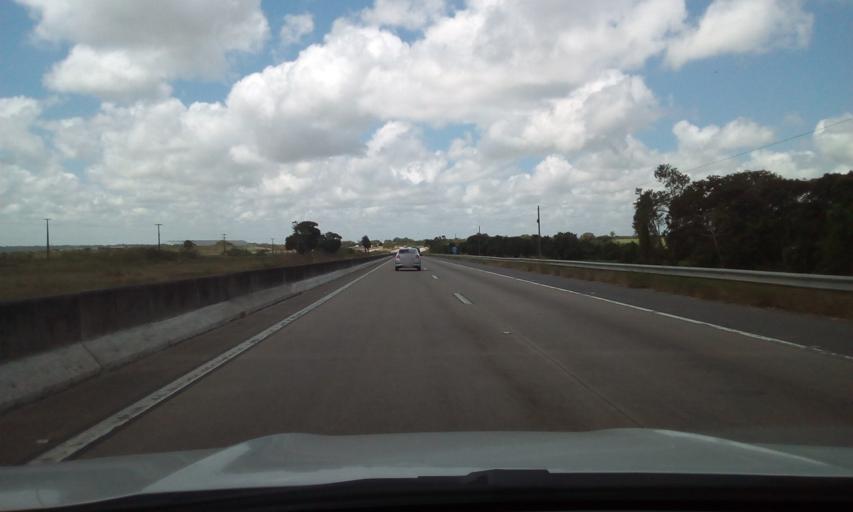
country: BR
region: Pernambuco
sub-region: Itapissuma
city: Itapissuma
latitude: -7.7303
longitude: -34.9414
